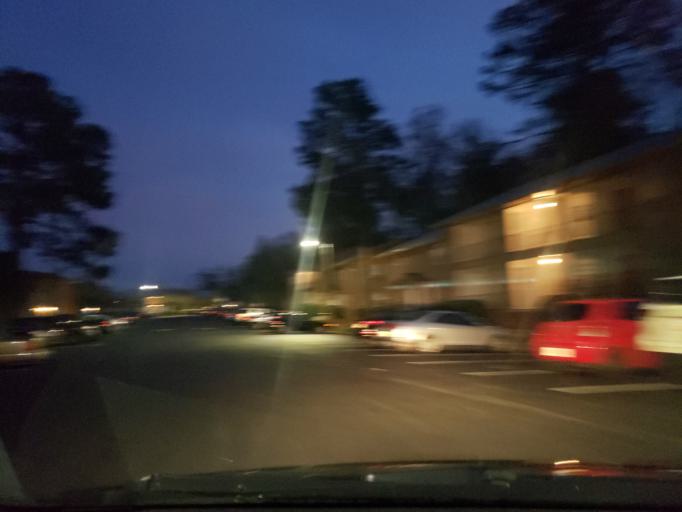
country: US
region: Georgia
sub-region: Chatham County
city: Montgomery
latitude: 31.9894
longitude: -81.1358
